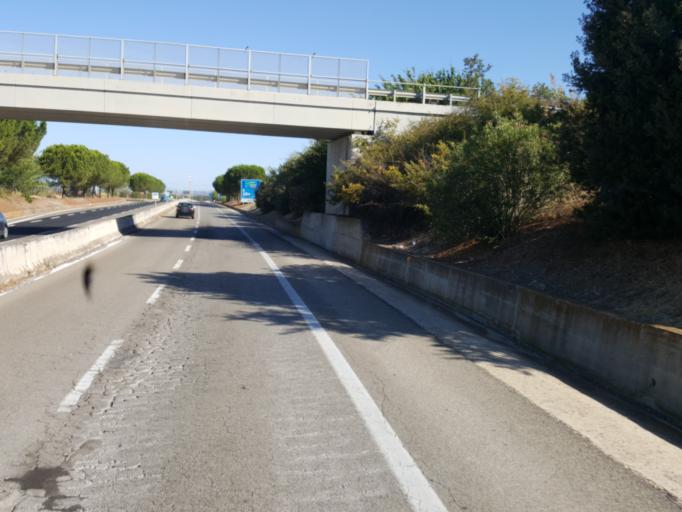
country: IT
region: Latium
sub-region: Citta metropolitana di Roma Capitale
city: Aurelia
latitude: 42.1526
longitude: 11.7917
